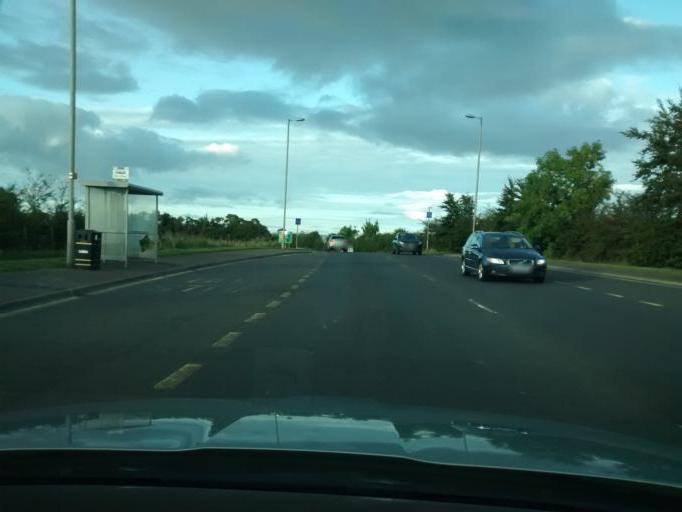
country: GB
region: Scotland
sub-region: Renfrewshire
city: Lochwinnoch
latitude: 55.7861
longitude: -4.6065
